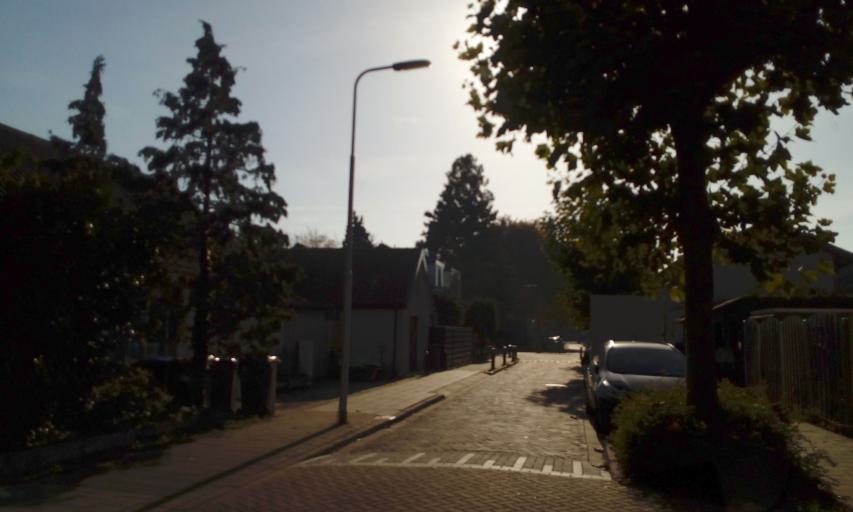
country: NL
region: South Holland
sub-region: Gemeente Lansingerland
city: Bleiswijk
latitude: 52.0083
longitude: 4.5313
